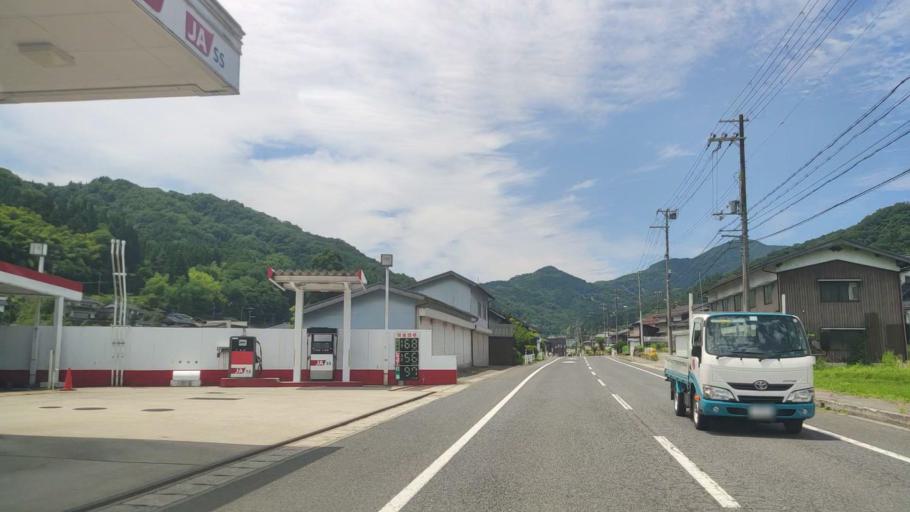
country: JP
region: Hyogo
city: Toyooka
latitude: 35.4647
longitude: 134.5450
